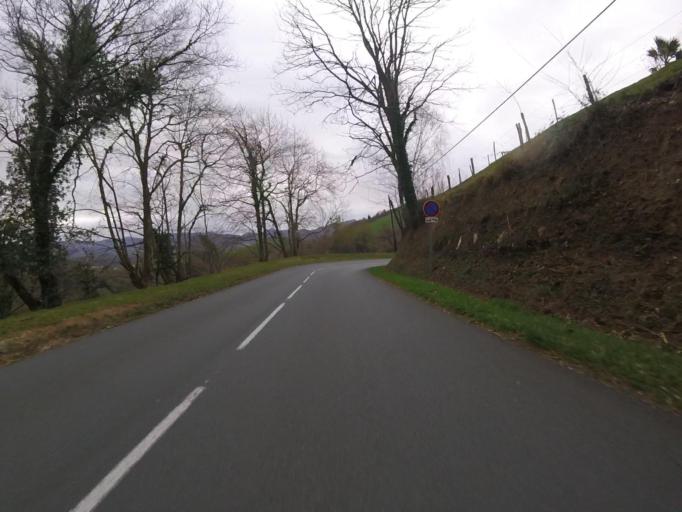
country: FR
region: Aquitaine
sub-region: Departement des Pyrenees-Atlantiques
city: Sare
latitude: 43.3208
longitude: -1.5980
